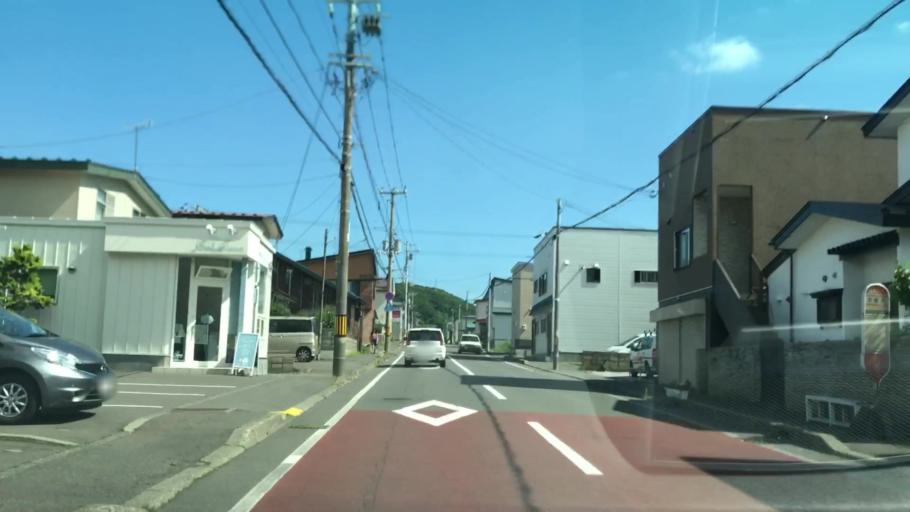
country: JP
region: Hokkaido
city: Muroran
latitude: 42.3126
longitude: 140.9918
